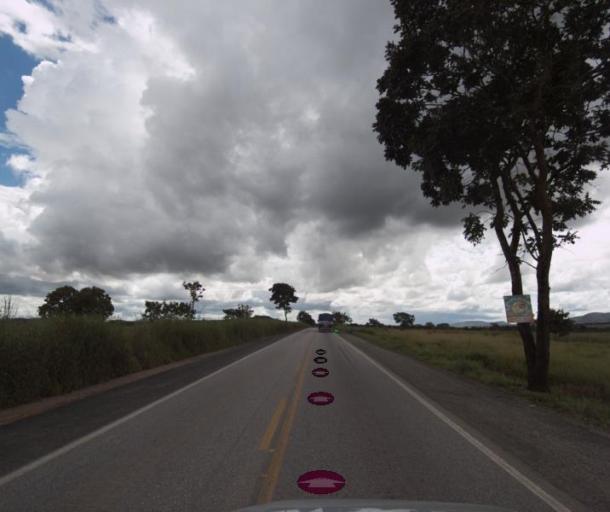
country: BR
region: Goias
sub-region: Uruacu
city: Uruacu
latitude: -14.2609
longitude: -49.1425
